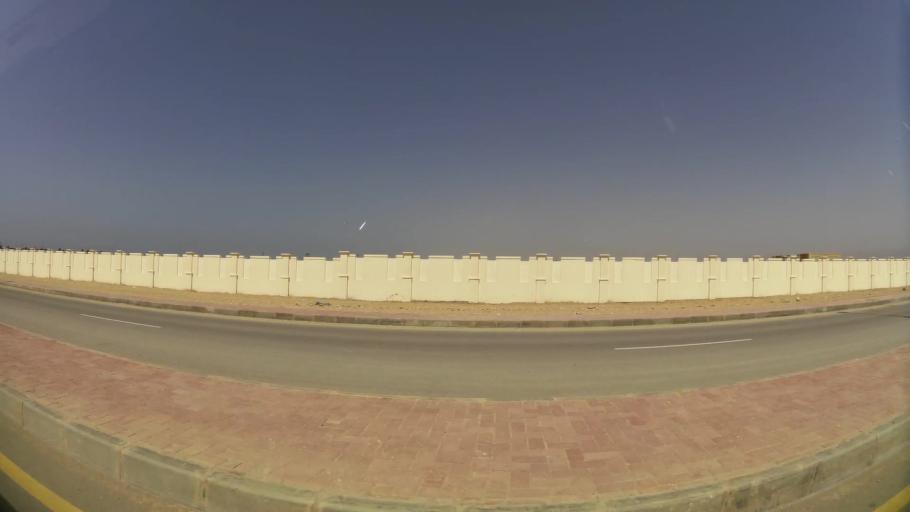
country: OM
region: Zufar
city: Salalah
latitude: 17.0331
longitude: 54.1346
